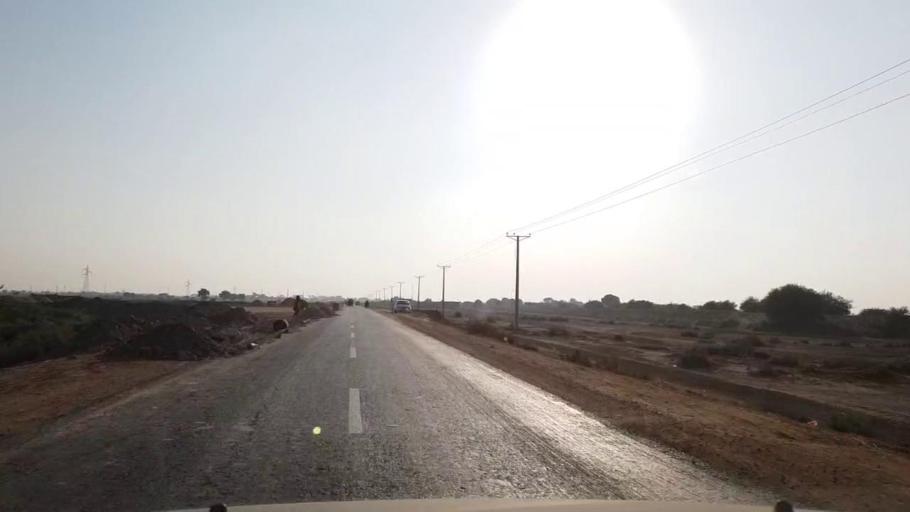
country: PK
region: Sindh
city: Mirpur Batoro
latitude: 24.7538
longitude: 68.2685
